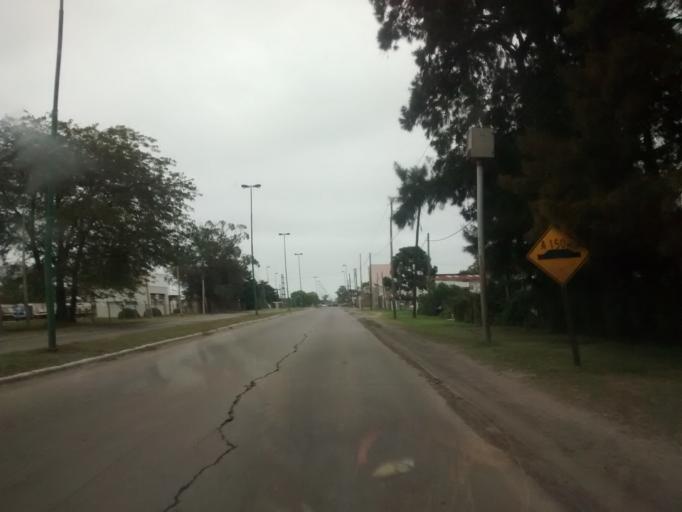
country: AR
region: Buenos Aires
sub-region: Partido de La Plata
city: La Plata
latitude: -34.9798
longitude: -58.0314
